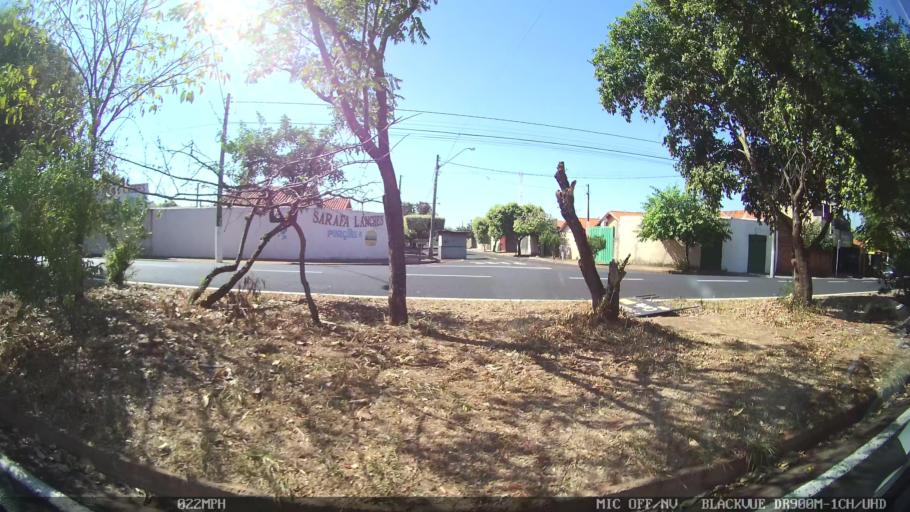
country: BR
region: Sao Paulo
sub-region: Sao Jose Do Rio Preto
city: Sao Jose do Rio Preto
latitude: -20.7491
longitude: -49.4073
